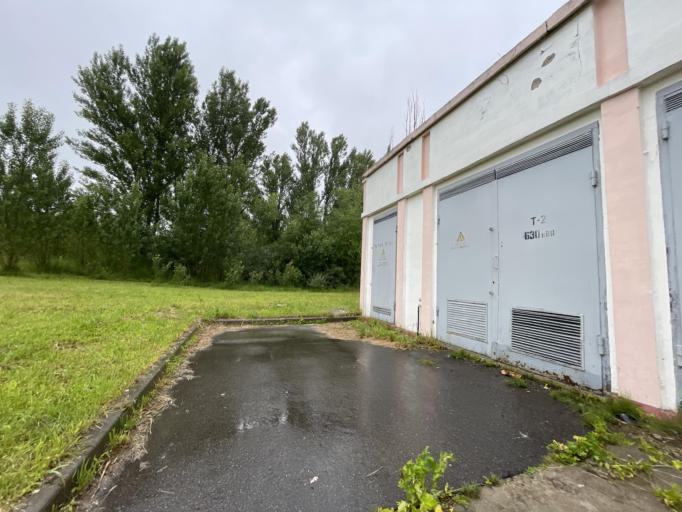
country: BY
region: Grodnenskaya
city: Hrodna
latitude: 53.7014
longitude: 23.8277
